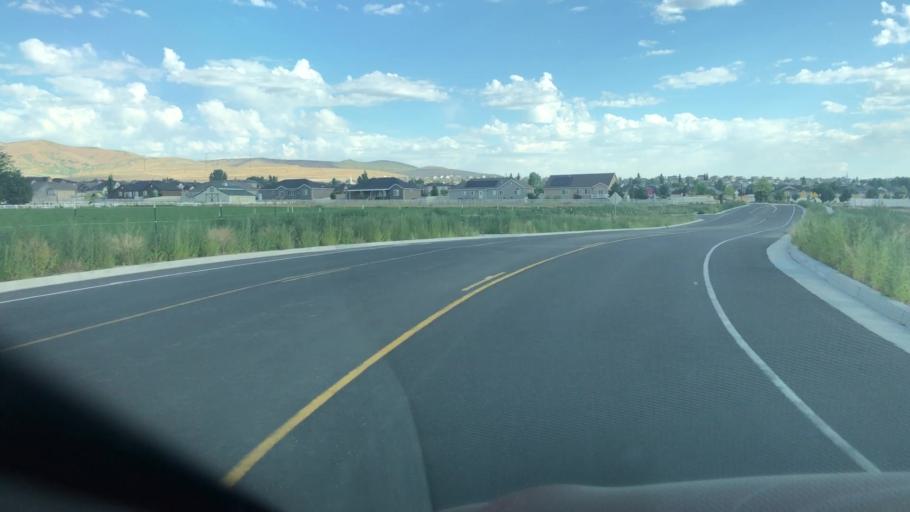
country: US
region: Utah
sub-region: Utah County
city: Saratoga Springs
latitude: 40.3894
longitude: -111.9259
